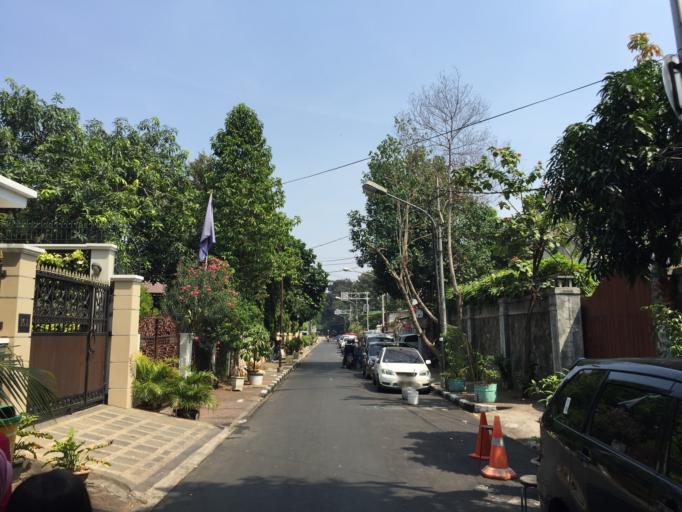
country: ID
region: Jakarta Raya
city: Jakarta
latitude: -6.2041
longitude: 106.8382
